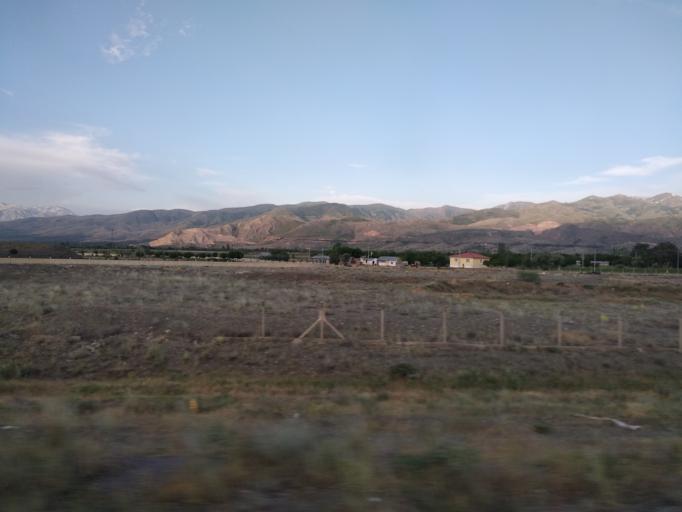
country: TR
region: Erzincan
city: Catalarmut
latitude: 39.8012
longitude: 39.3751
